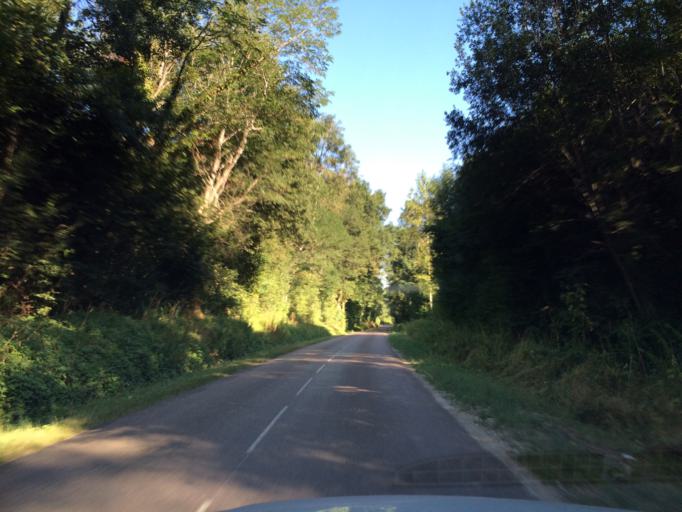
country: FR
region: Bourgogne
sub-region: Departement de l'Yonne
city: Fleury-la-Vallee
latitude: 47.8845
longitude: 3.4395
